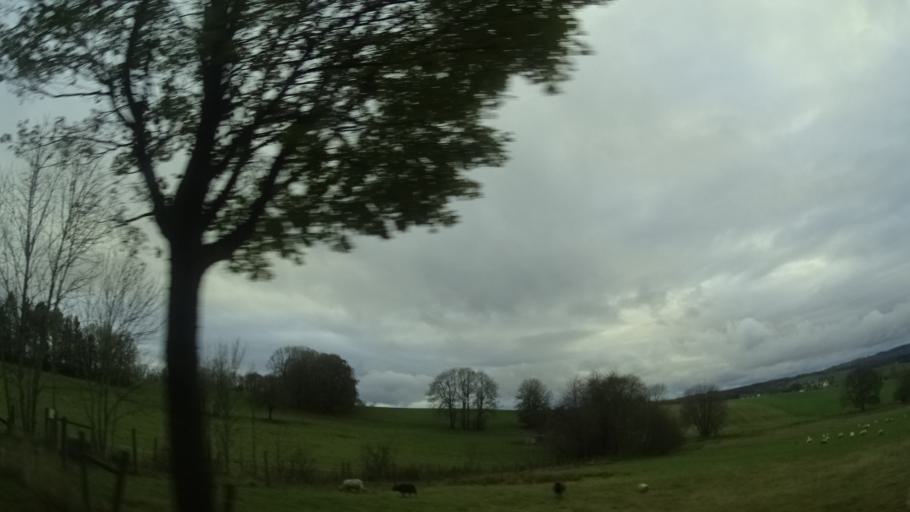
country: DE
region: Hesse
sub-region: Regierungsbezirk Giessen
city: Freiensteinau
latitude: 50.4597
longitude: 9.3897
